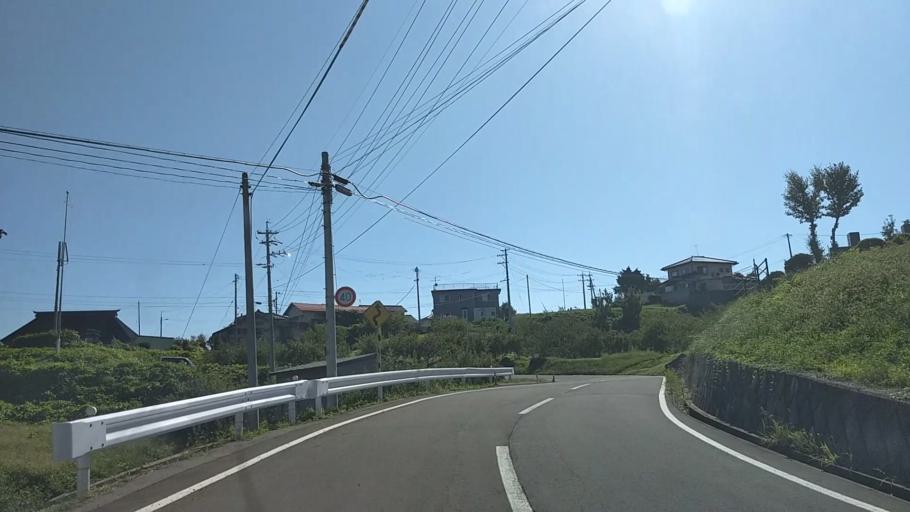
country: JP
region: Nagano
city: Nagano-shi
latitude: 36.5777
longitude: 138.1186
